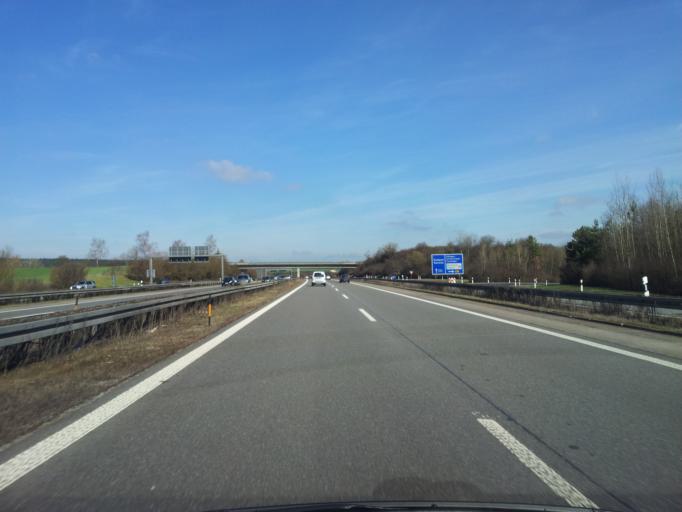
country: DE
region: Baden-Wuerttemberg
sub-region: Freiburg Region
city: Deisslingen
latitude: 48.0911
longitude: 8.5924
